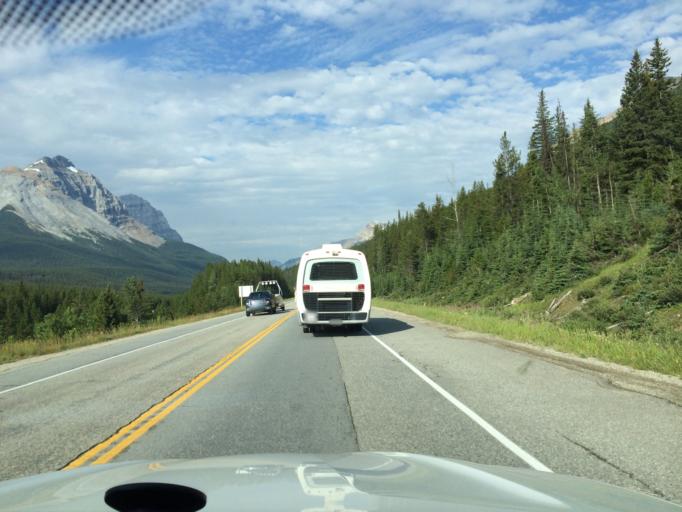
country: CA
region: Alberta
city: Lake Louise
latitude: 51.4493
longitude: -116.3181
